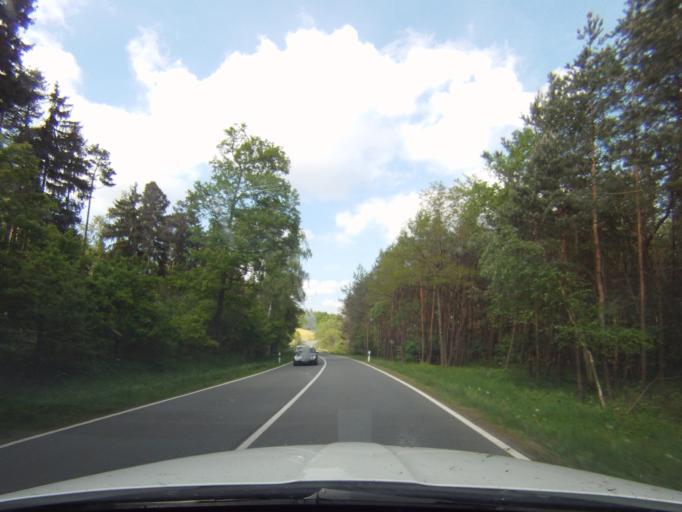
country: DE
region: Thuringia
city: Mittelpollnitz
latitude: 50.7732
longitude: 11.9337
